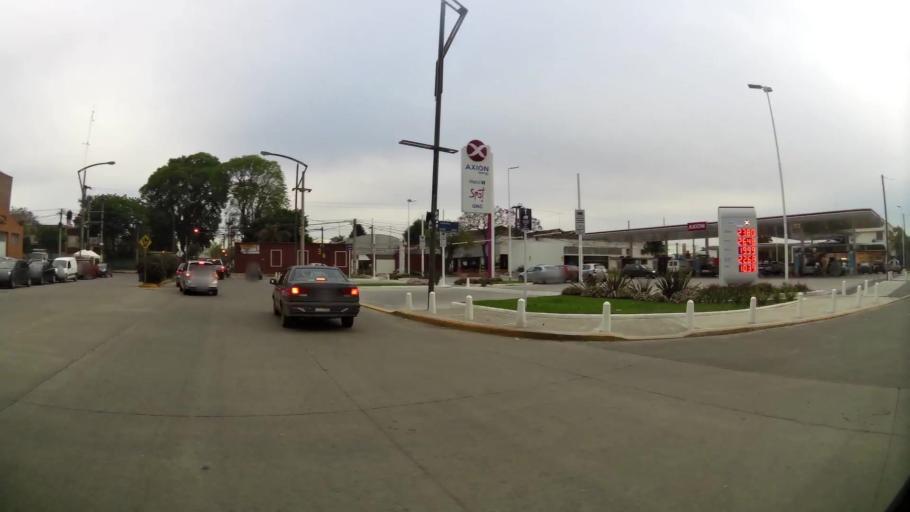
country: AR
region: Santa Fe
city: Granadero Baigorria
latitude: -32.8933
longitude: -60.7065
